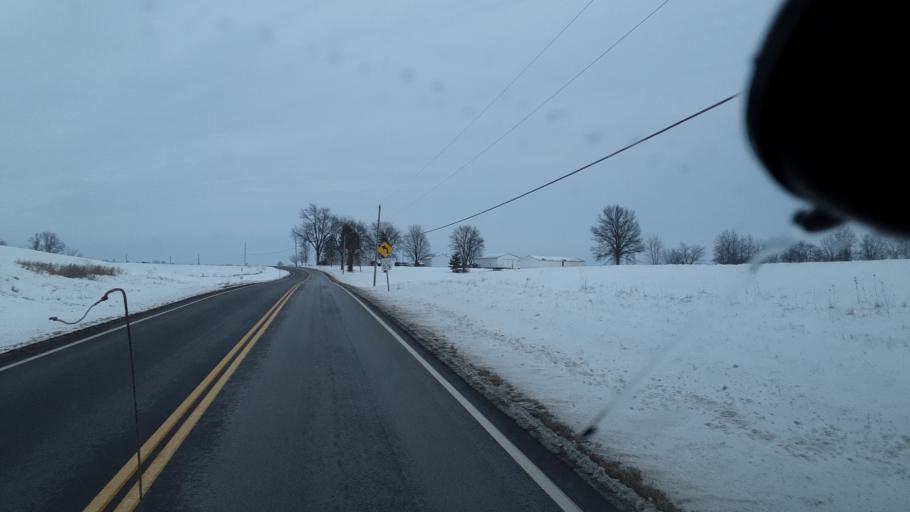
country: US
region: Ohio
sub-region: Union County
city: New California
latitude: 40.2120
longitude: -83.2619
